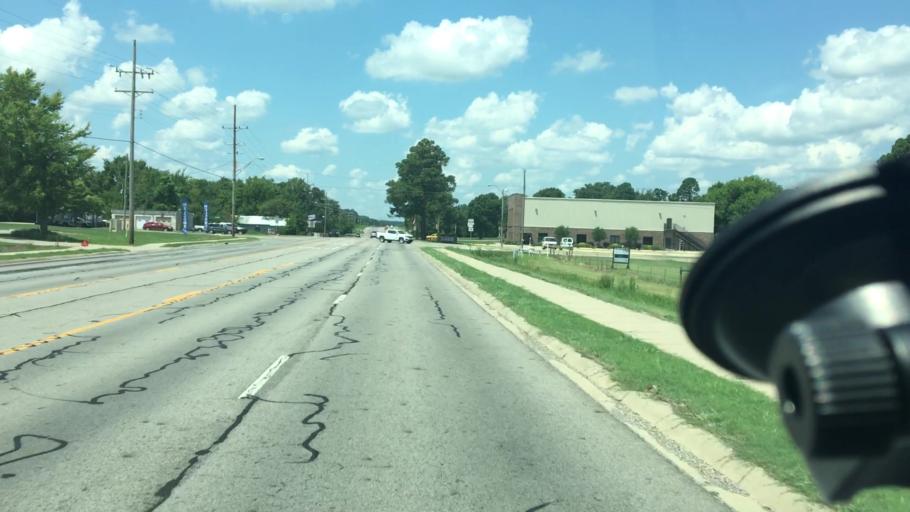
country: US
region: Arkansas
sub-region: Sebastian County
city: Barling
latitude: 35.3194
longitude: -94.2512
